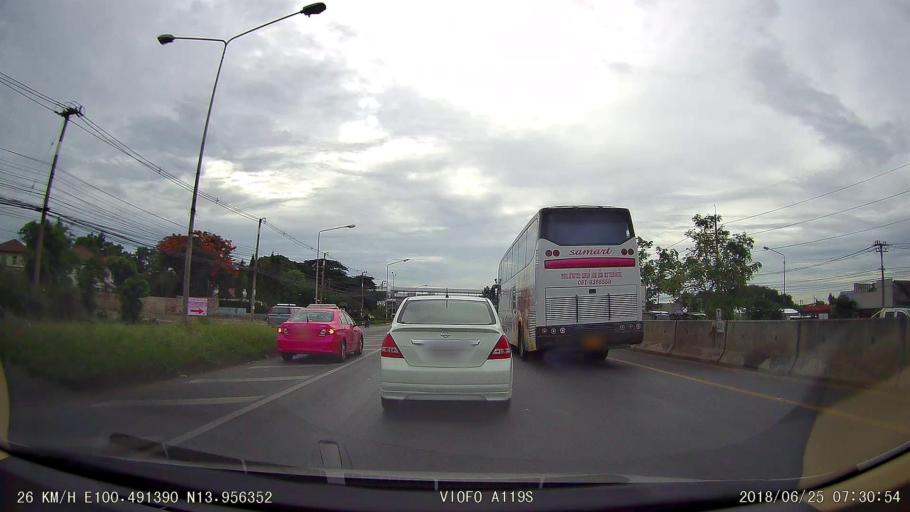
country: TH
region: Nonthaburi
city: Pak Kret
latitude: 13.9564
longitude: 100.4914
